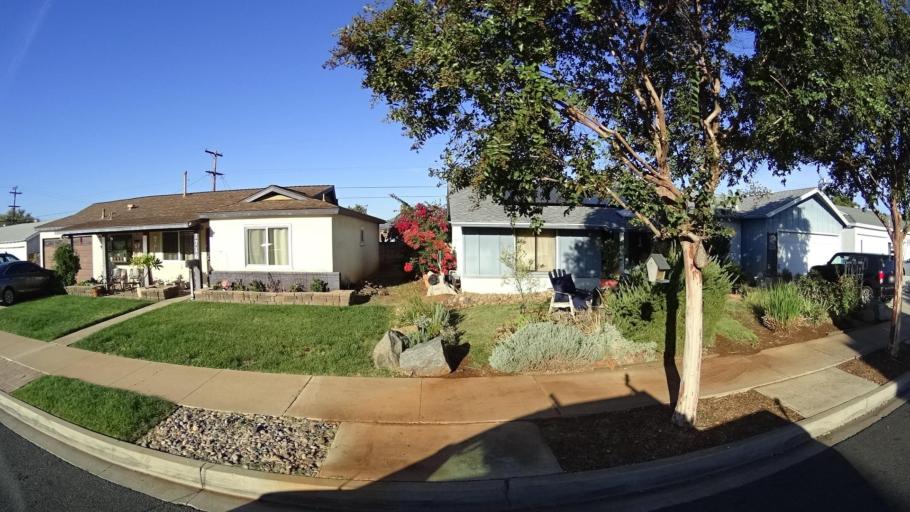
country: US
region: California
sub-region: San Diego County
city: Bostonia
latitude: 32.8196
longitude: -116.9488
